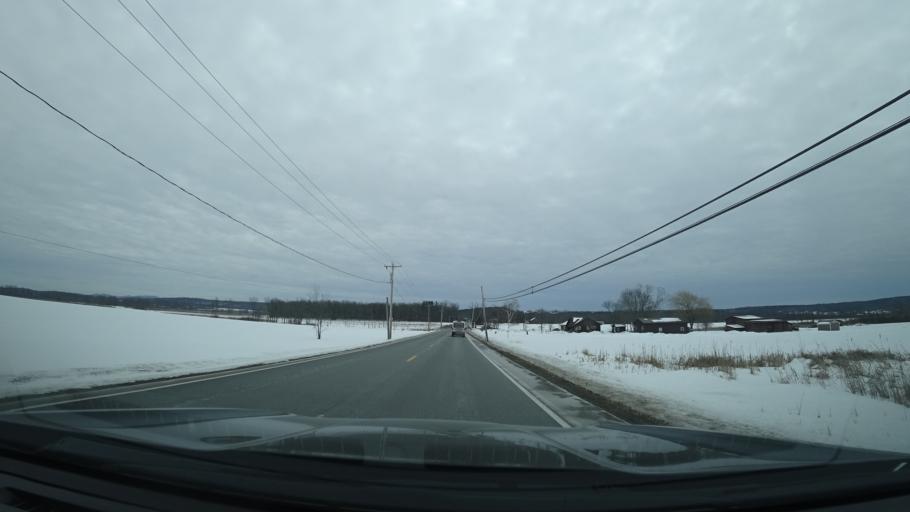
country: US
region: New York
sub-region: Washington County
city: Fort Edward
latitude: 43.2635
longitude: -73.5349
